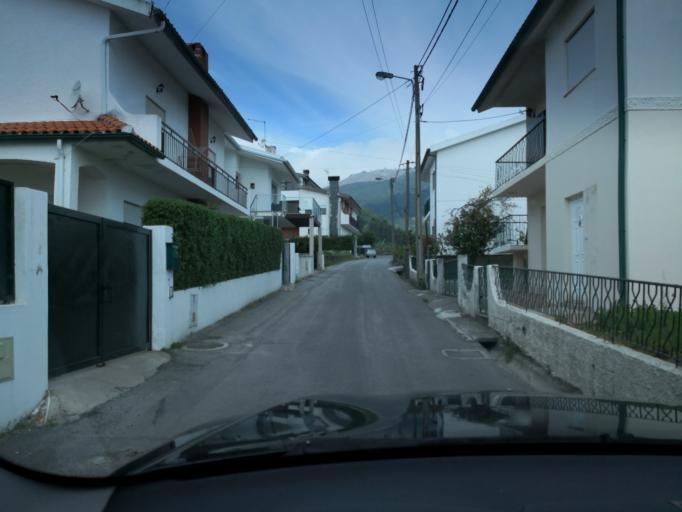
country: PT
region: Vila Real
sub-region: Vila Real
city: Vila Real
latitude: 41.3183
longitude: -7.7710
